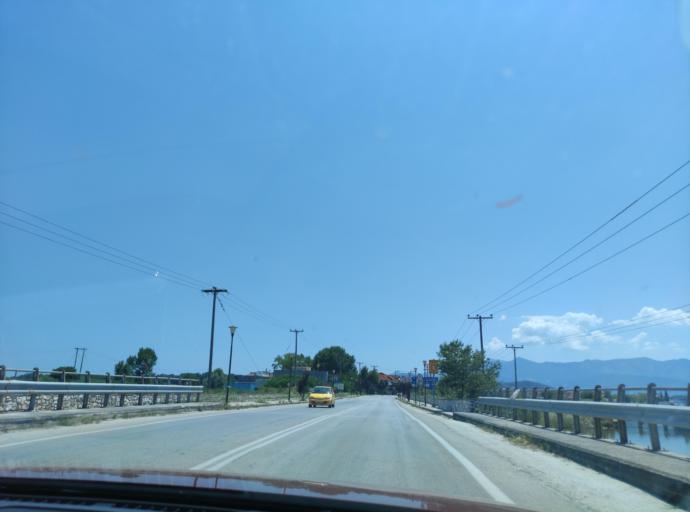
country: GR
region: East Macedonia and Thrace
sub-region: Nomos Kavalas
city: Keramoti
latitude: 40.8656
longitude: 24.7054
